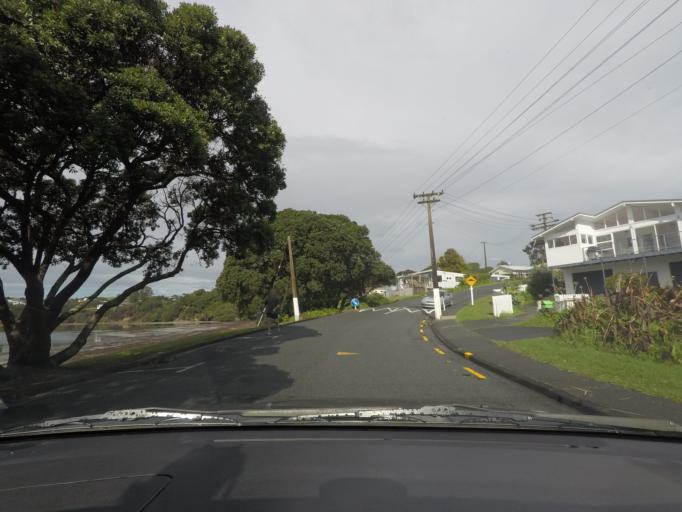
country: NZ
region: Auckland
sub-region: Auckland
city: Warkworth
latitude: -36.4225
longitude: 174.7309
